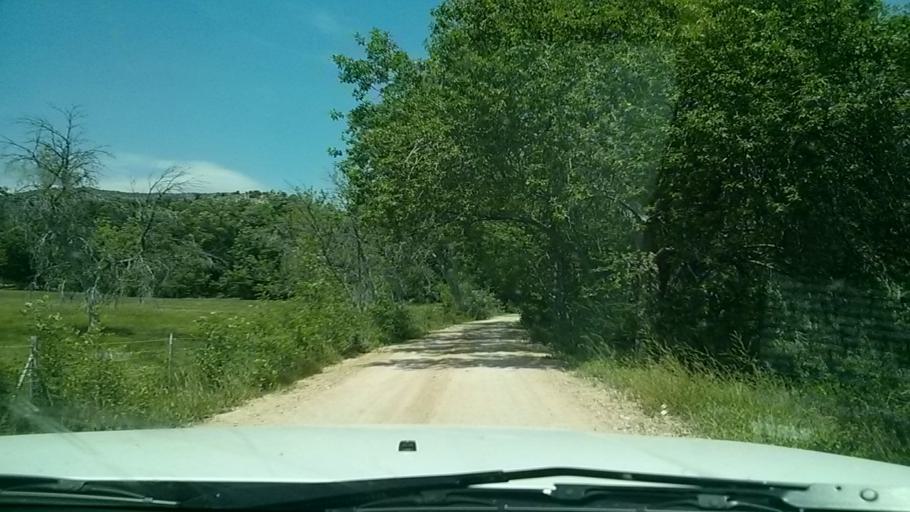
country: US
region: Utah
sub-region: Washington County
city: Toquerville
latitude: 37.2565
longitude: -113.4280
